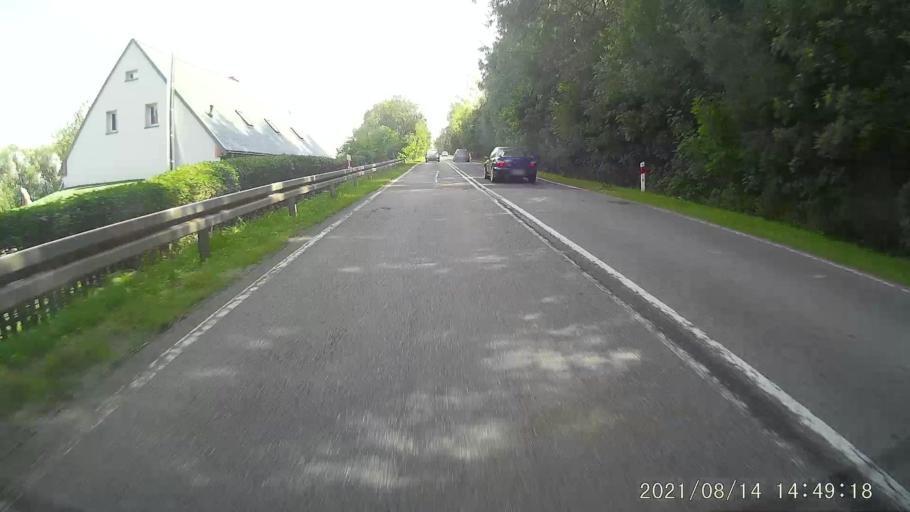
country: PL
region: Lower Silesian Voivodeship
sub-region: Powiat walbrzyski
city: Gluszyca Gorna
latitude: 50.6403
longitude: 16.3869
